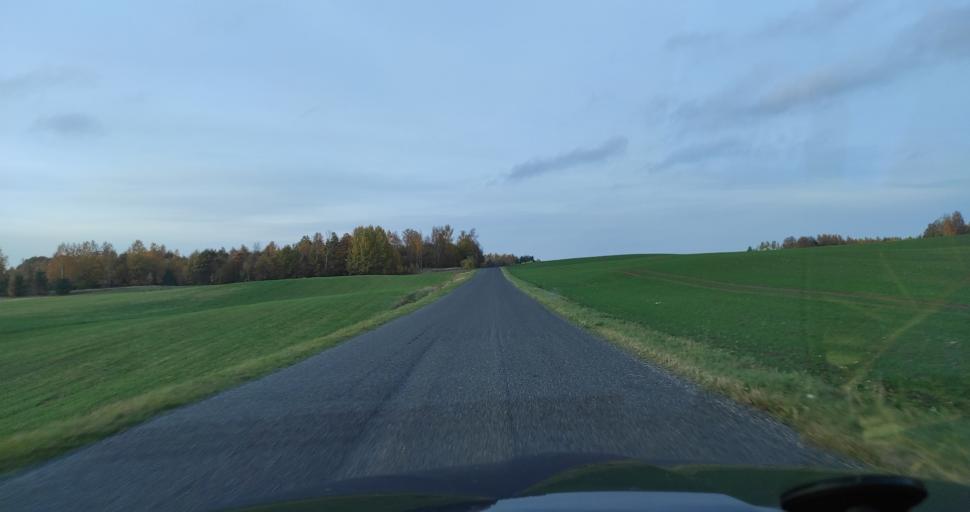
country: LV
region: Aizpute
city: Aizpute
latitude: 56.7043
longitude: 21.7941
